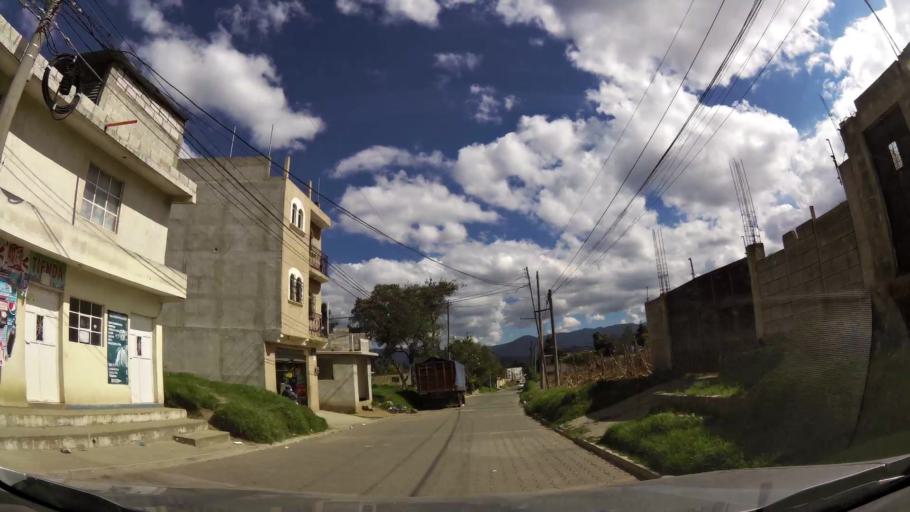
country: GT
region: Quetzaltenango
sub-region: Municipio de La Esperanza
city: La Esperanza
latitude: 14.8462
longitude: -91.5482
